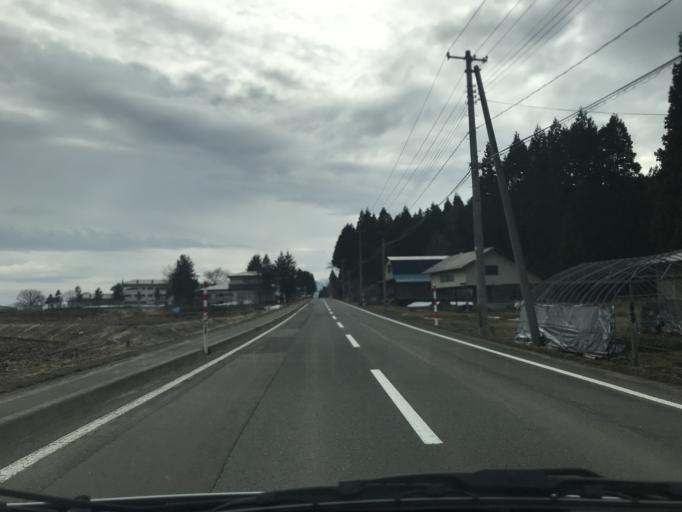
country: JP
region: Iwate
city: Hanamaki
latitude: 39.3576
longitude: 140.9899
